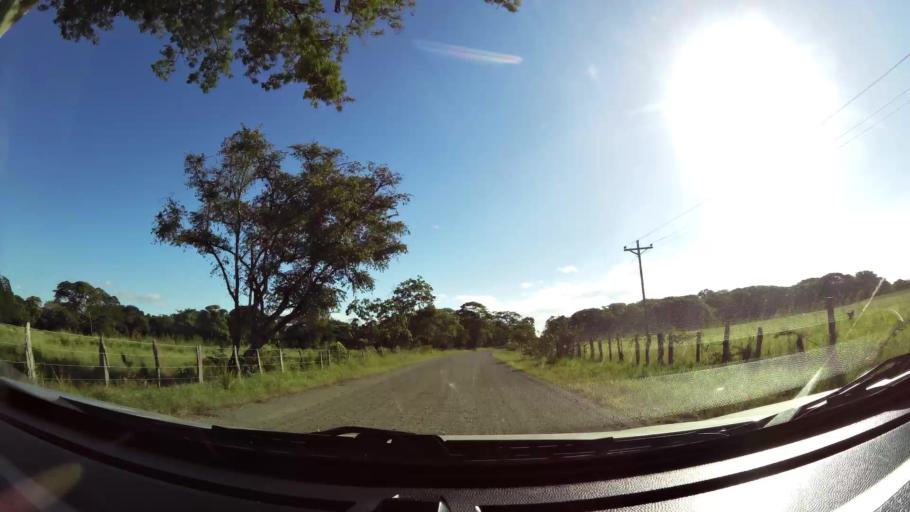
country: CR
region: Guanacaste
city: Sardinal
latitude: 10.4854
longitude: -85.5830
